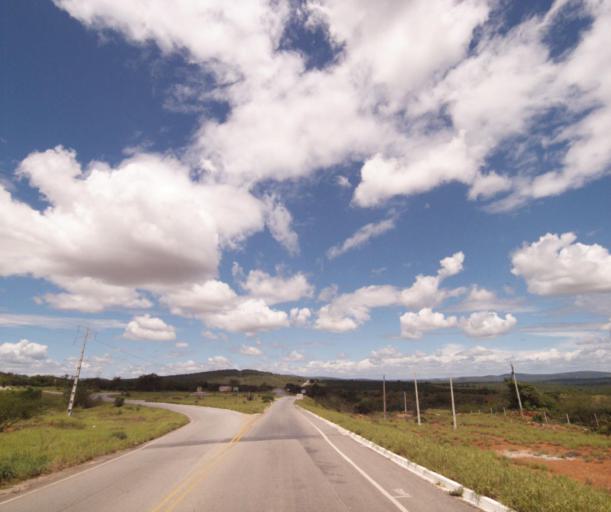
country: BR
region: Bahia
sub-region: Brumado
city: Brumado
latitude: -14.2380
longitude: -41.7159
